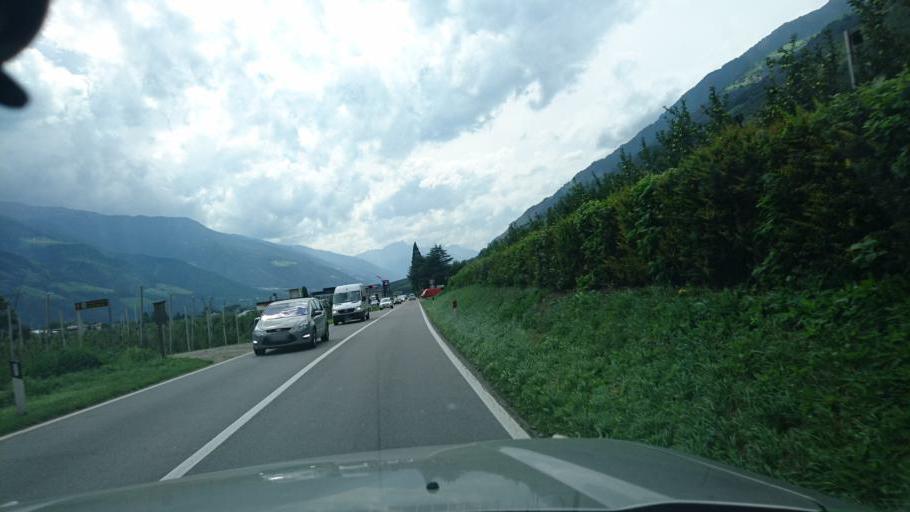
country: IT
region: Trentino-Alto Adige
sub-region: Bolzano
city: Plaus
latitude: 46.6637
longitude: 11.0452
